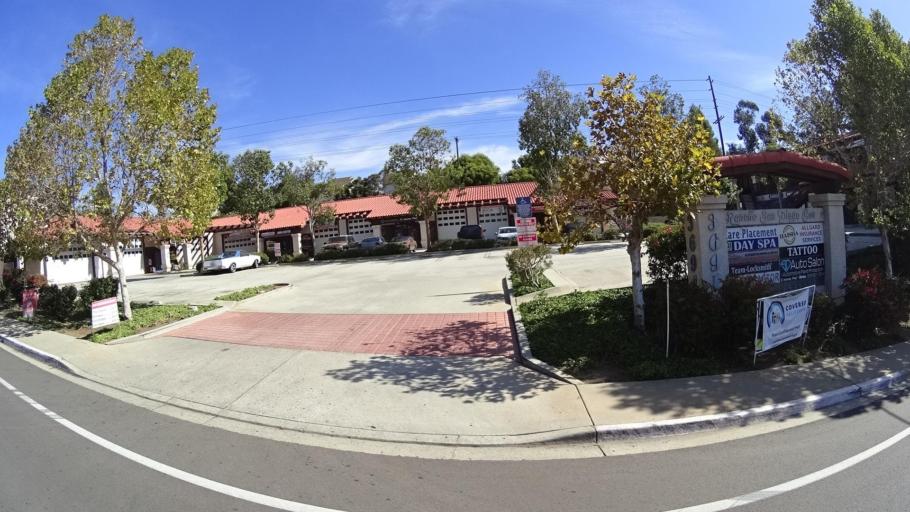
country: US
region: California
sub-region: San Diego County
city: Casa de Oro-Mount Helix
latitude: 32.7471
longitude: -116.9579
